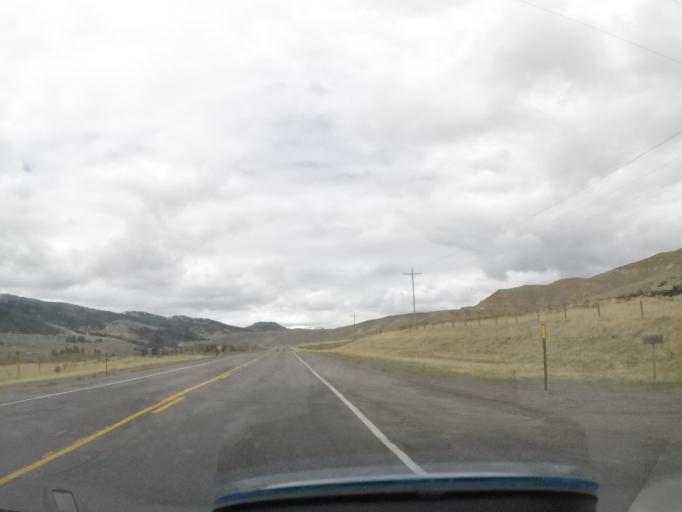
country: US
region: Wyoming
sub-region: Sublette County
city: Pinedale
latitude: 43.5724
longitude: -109.7238
